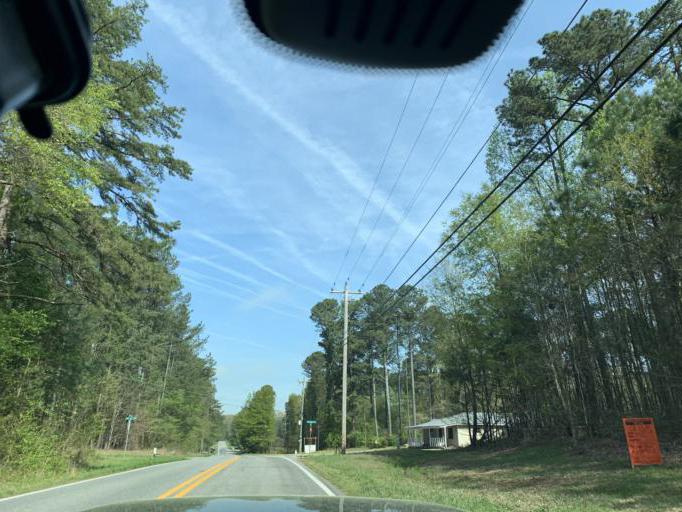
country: US
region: Georgia
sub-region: Forsyth County
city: Cumming
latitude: 34.2134
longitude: -84.0764
